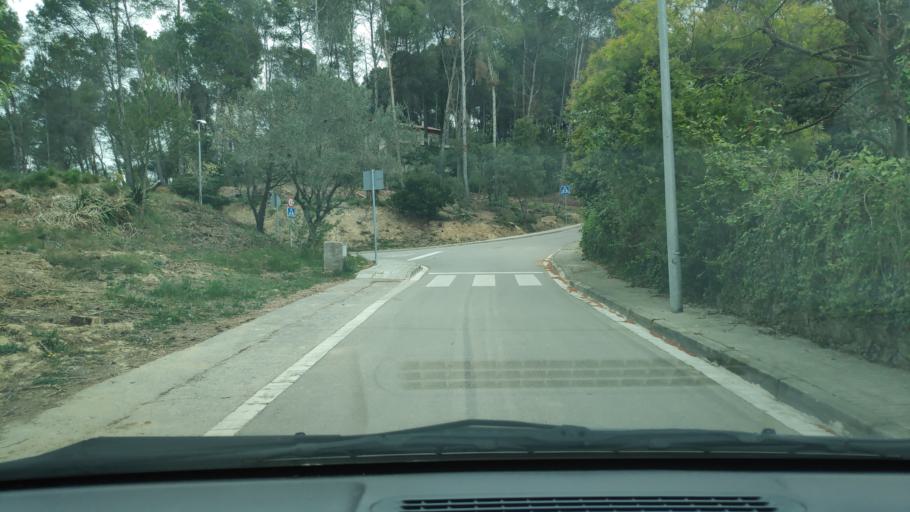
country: ES
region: Catalonia
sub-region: Provincia de Barcelona
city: Rubi
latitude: 41.5109
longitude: 2.0588
